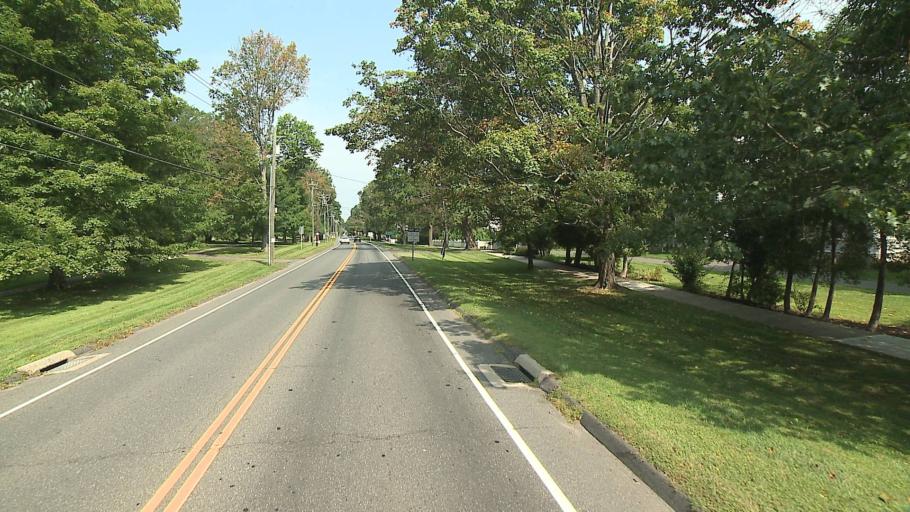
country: US
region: Connecticut
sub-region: Fairfield County
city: Ridgefield
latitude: 41.2741
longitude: -73.4973
